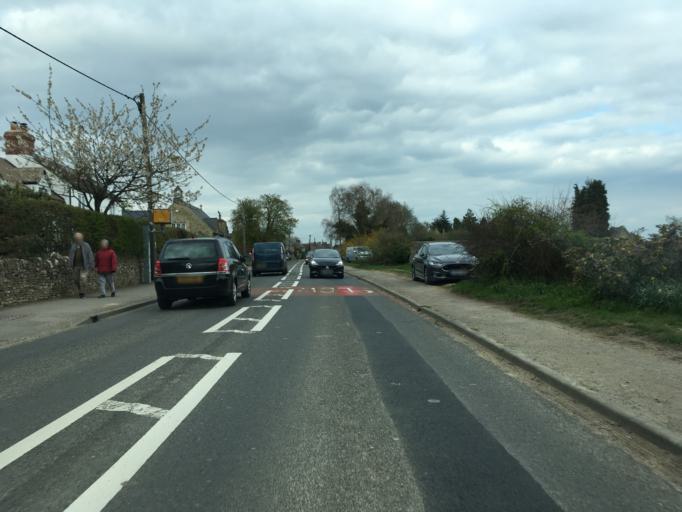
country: GB
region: England
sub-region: Oxfordshire
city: Woodstock
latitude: 51.8246
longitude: -1.3876
